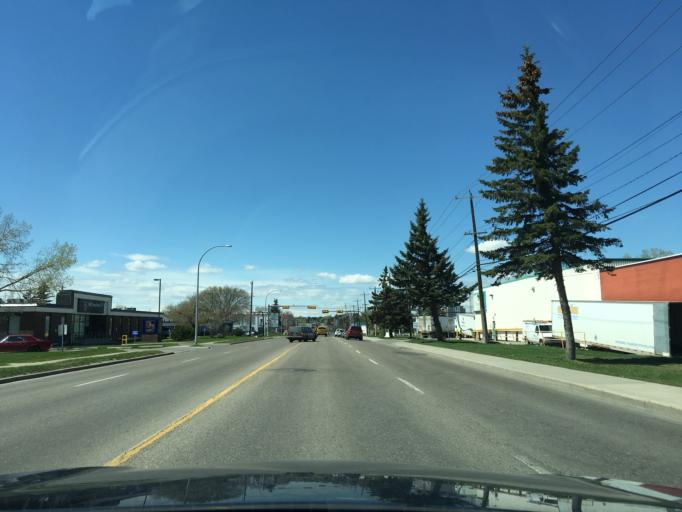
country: CA
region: Alberta
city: Calgary
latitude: 51.0014
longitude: -114.0552
